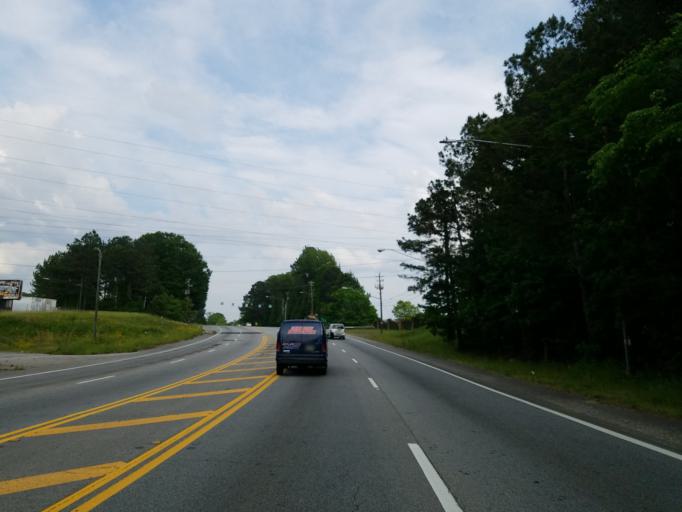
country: US
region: Georgia
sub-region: Cobb County
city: Mableton
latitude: 33.7946
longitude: -84.5059
